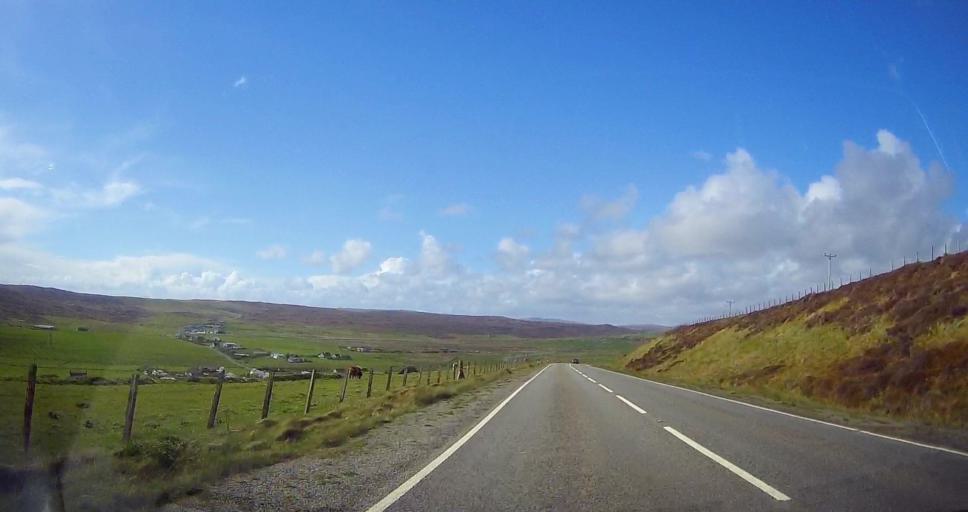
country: GB
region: Scotland
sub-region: Shetland Islands
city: Lerwick
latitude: 60.1782
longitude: -1.2239
